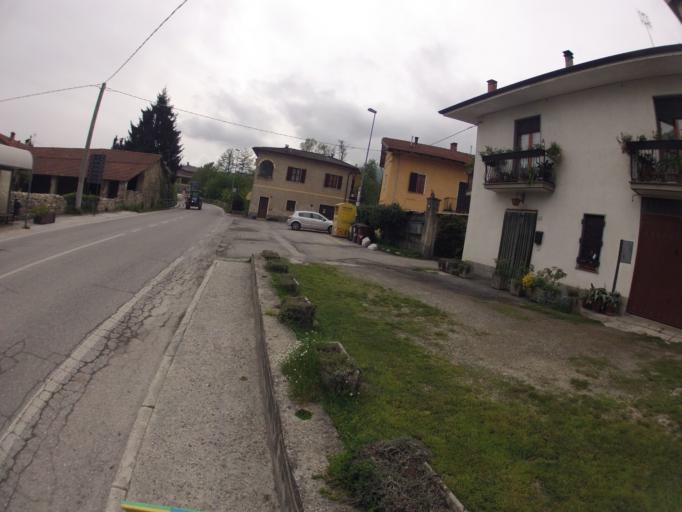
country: IT
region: Piedmont
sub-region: Provincia di Cuneo
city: Peveragno
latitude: 44.3303
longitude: 7.6115
